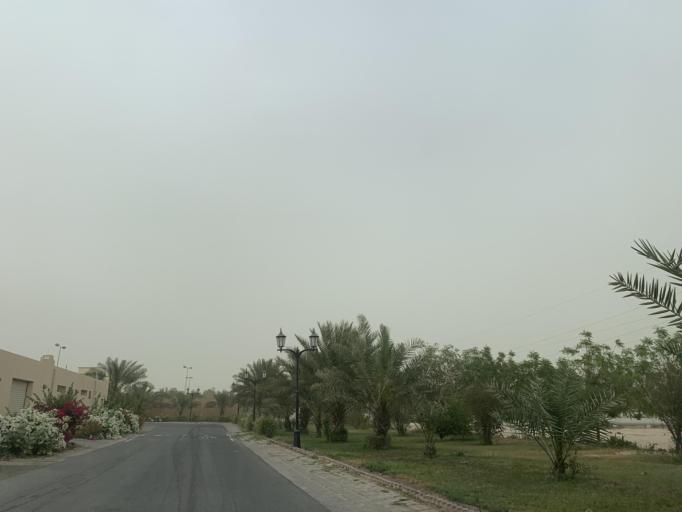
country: BH
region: Northern
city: Ar Rifa'
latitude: 26.1373
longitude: 50.5354
